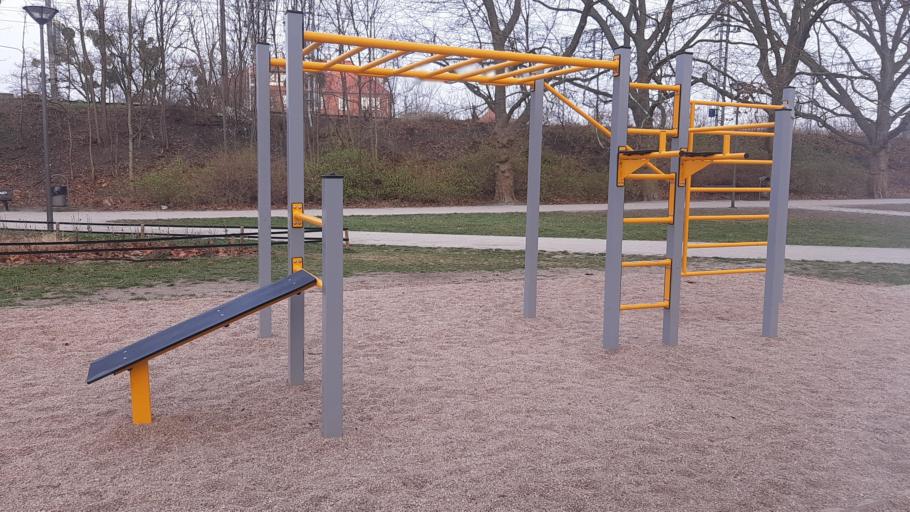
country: PL
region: Lower Silesian Voivodeship
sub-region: Powiat wroclawski
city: Wroclaw
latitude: 51.0904
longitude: 16.9965
